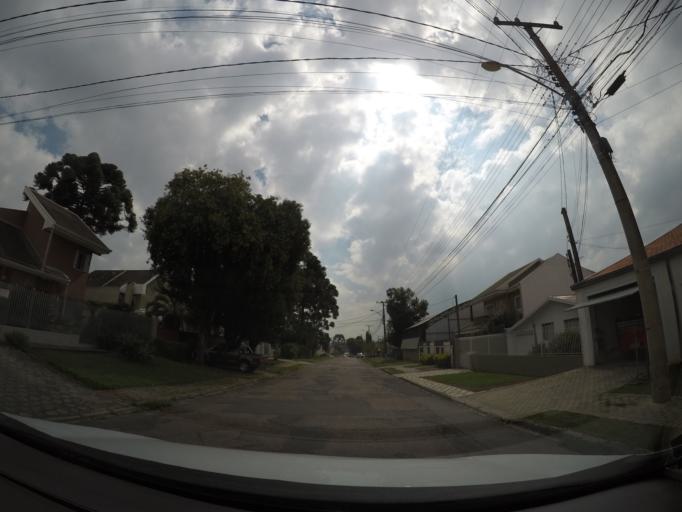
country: BR
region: Parana
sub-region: Sao Jose Dos Pinhais
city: Sao Jose dos Pinhais
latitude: -25.4967
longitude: -49.2495
